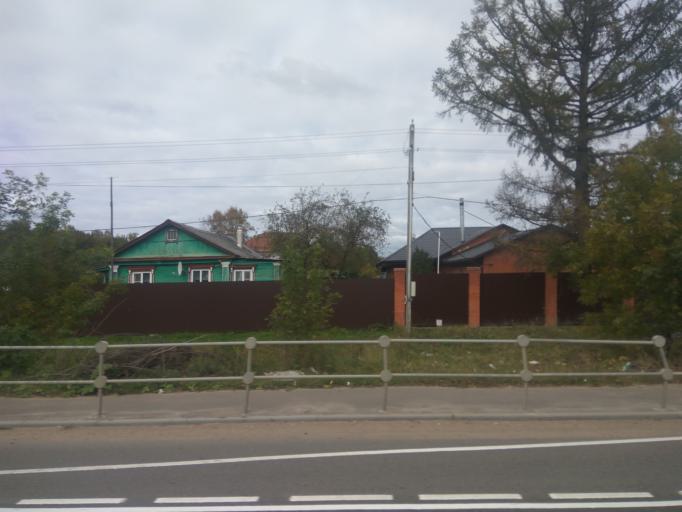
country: RU
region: Moskovskaya
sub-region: Shchelkovskiy Rayon
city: Grebnevo
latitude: 55.9793
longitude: 38.1161
